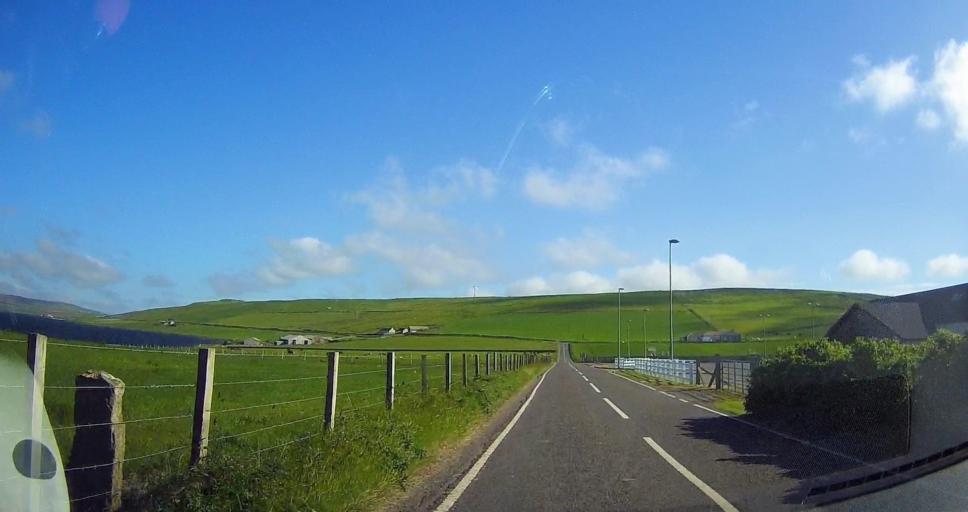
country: GB
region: Scotland
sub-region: Orkney Islands
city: Stromness
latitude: 59.1202
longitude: -3.3058
